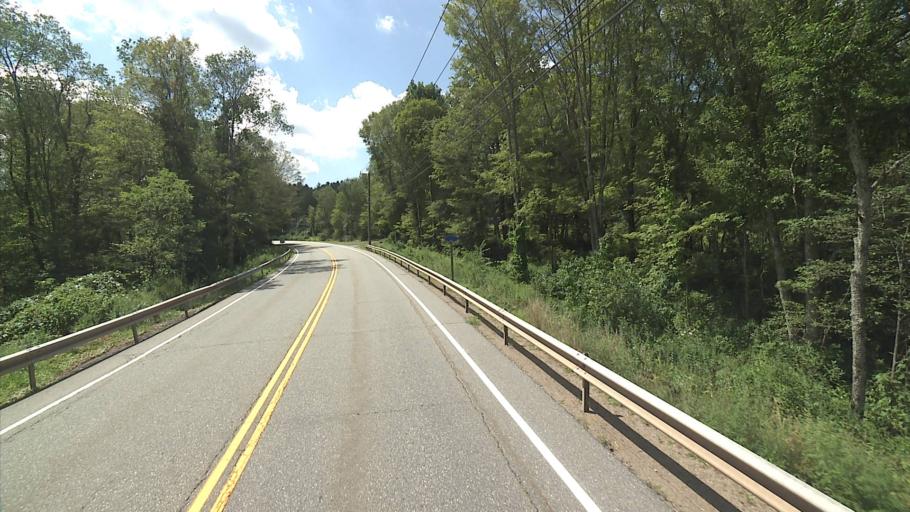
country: US
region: Connecticut
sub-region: Windham County
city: South Woodstock
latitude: 41.8667
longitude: -72.0928
